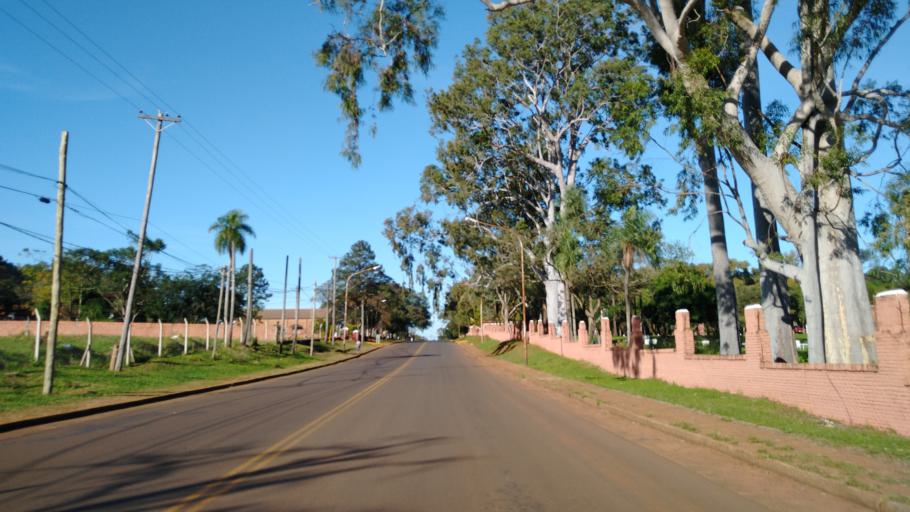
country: AR
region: Misiones
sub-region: Departamento de Capital
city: Posadas
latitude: -27.3619
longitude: -55.9191
